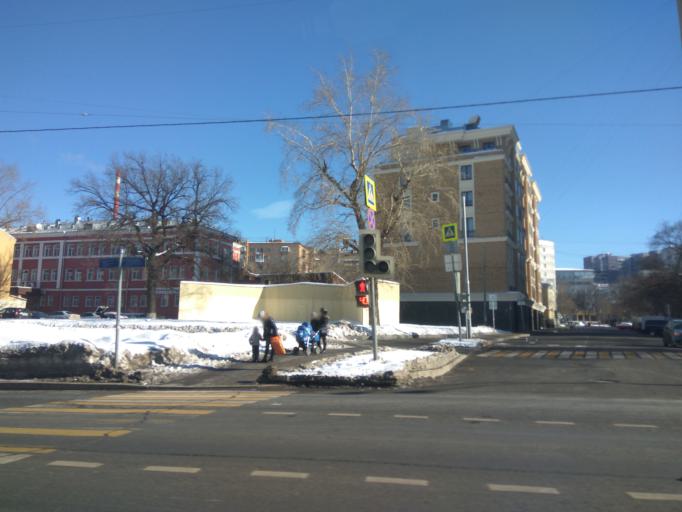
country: RU
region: Moscow
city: Taganskiy
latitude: 55.7331
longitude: 37.6588
